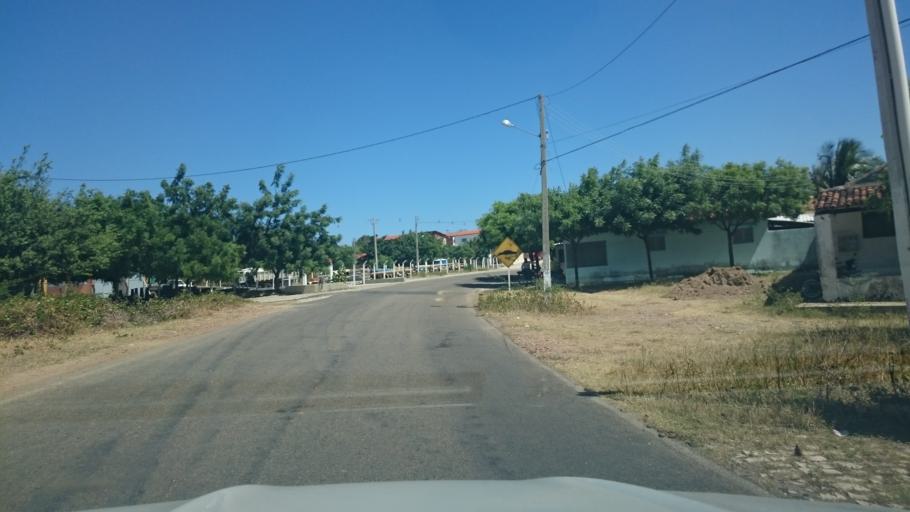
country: BR
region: Paraiba
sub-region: Catole Do Rocha
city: Sao Bento
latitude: -6.1583
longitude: -37.8358
